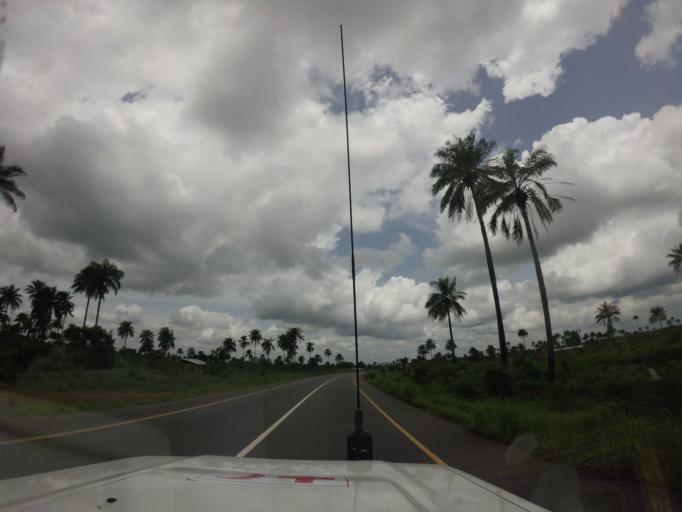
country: SL
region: Northern Province
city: Mange
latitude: 9.0057
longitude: -12.8594
